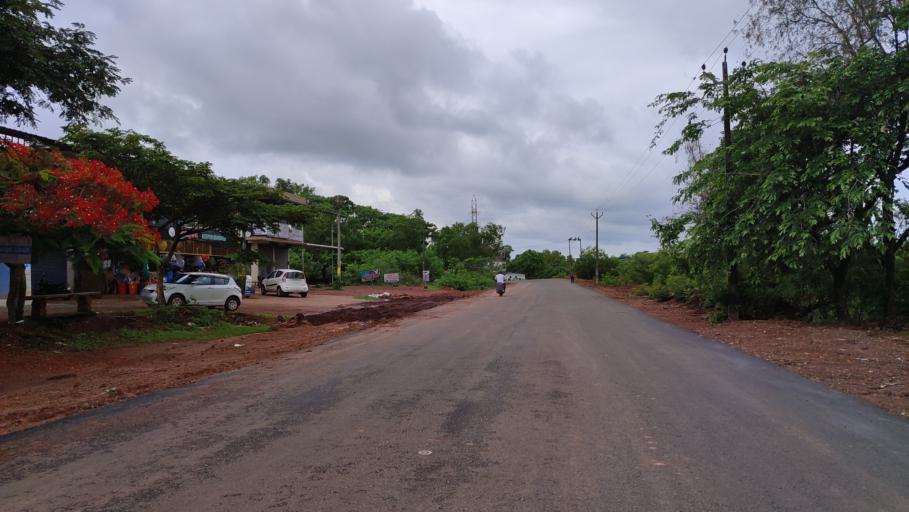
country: IN
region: Kerala
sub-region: Kasaragod District
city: Kasaragod
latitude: 12.5441
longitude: 75.0705
